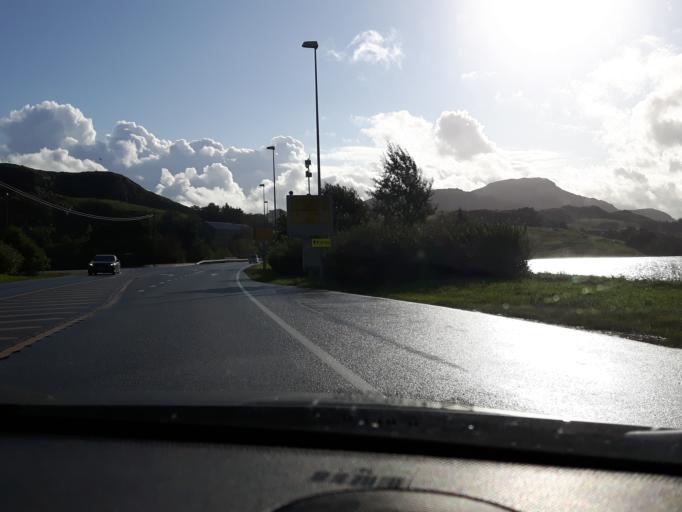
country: NO
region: Rogaland
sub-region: Gjesdal
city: Algard
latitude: 58.7656
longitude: 5.8807
